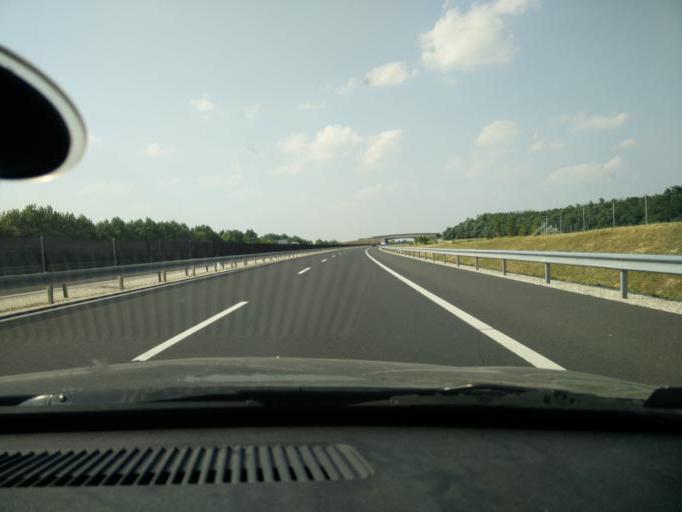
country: HU
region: Tolna
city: Szedres
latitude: 46.4509
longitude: 18.7058
